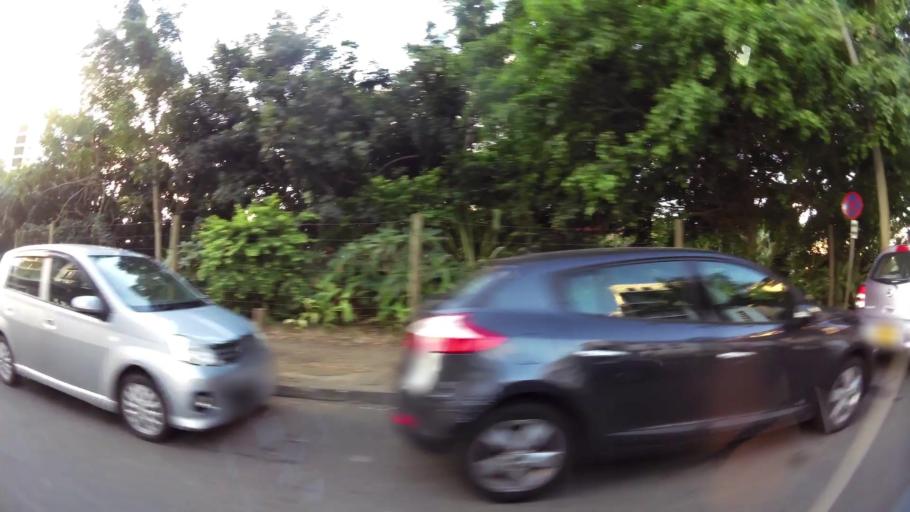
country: MU
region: Plaines Wilhems
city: Ebene
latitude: -20.2433
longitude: 57.4899
